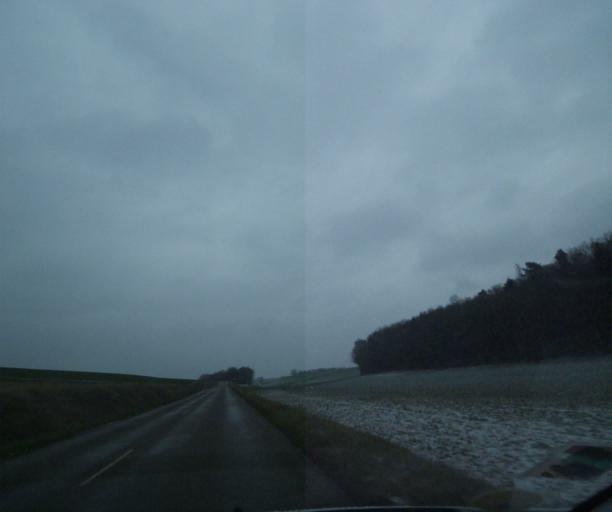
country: FR
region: Champagne-Ardenne
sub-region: Departement de la Haute-Marne
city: Wassy
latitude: 48.4345
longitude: 5.0251
